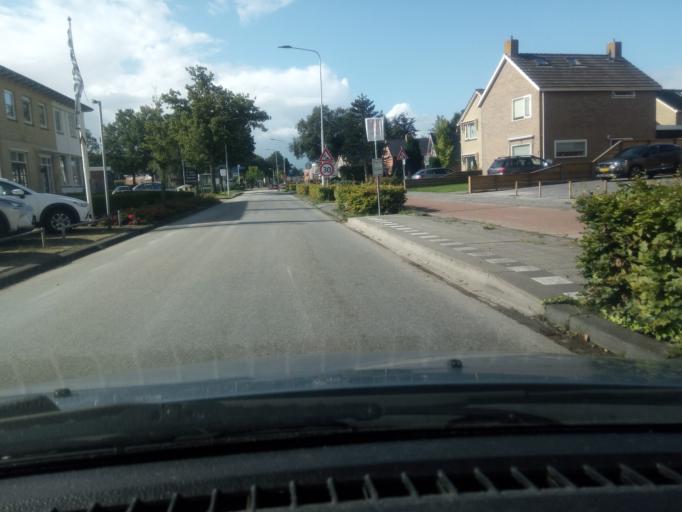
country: NL
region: Friesland
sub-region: Gemeente Achtkarspelen
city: Surhuisterveen
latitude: 53.1800
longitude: 6.1769
